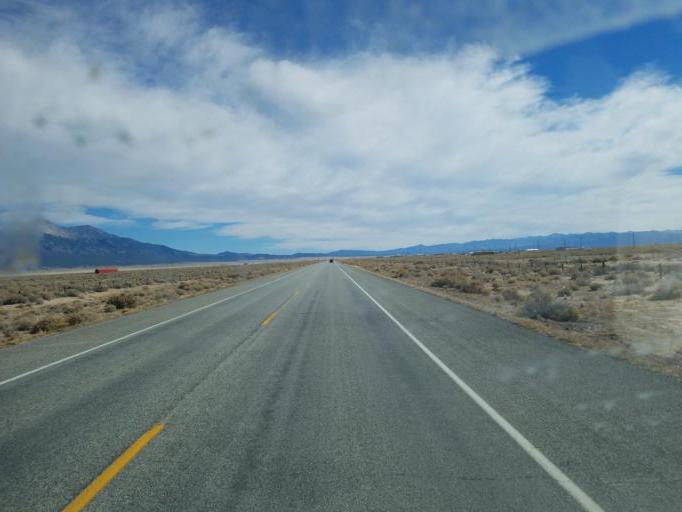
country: US
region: Colorado
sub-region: Alamosa County
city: Alamosa East
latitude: 37.4750
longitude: -105.7078
